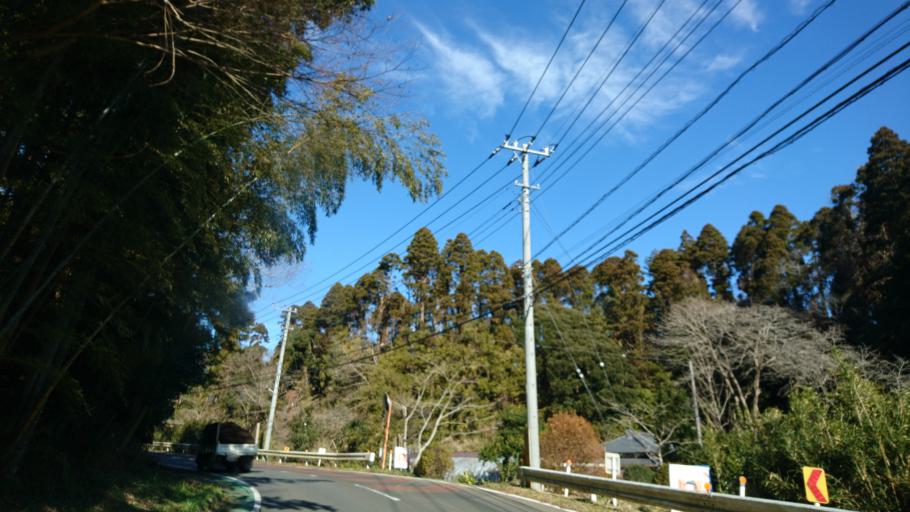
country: JP
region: Chiba
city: Yachimata
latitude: 35.6178
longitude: 140.3348
